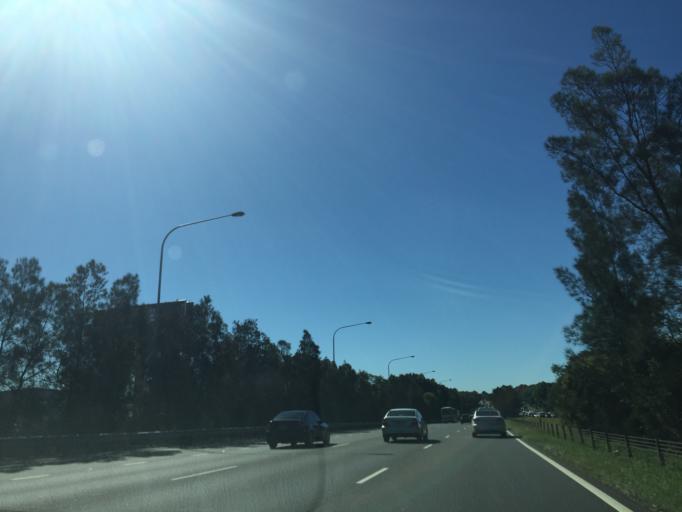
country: AU
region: New South Wales
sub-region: Auburn
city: Lidcombe
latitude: -33.8497
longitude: 151.0535
